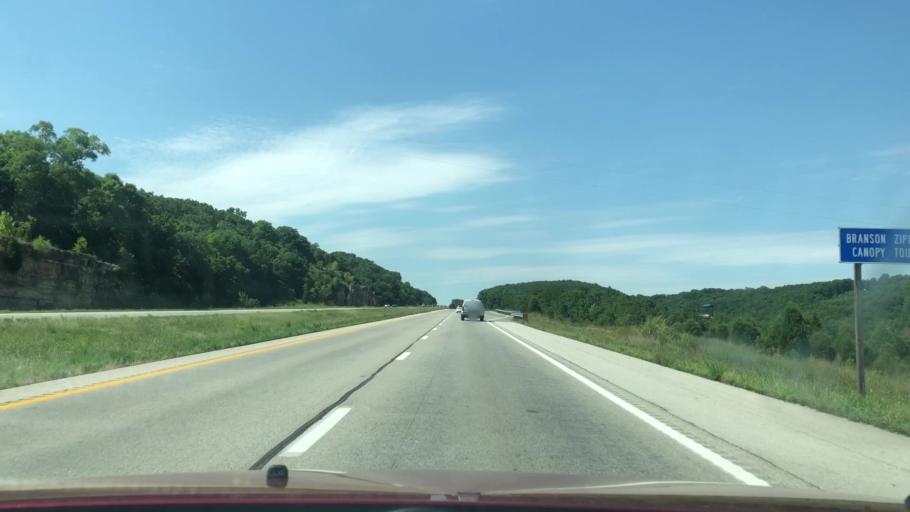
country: US
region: Missouri
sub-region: Taney County
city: Merriam Woods
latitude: 36.7786
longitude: -93.2244
